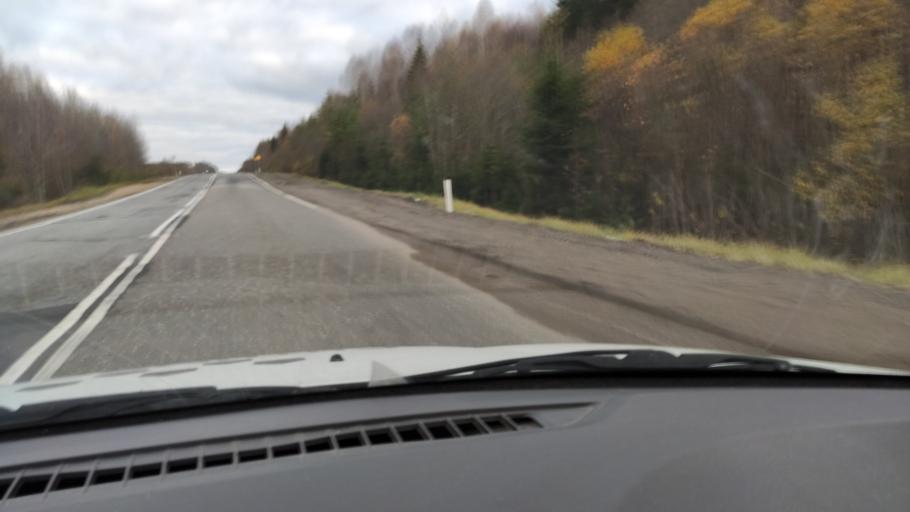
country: RU
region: Kirov
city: Chernaya Kholunitsa
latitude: 58.8903
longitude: 51.3549
